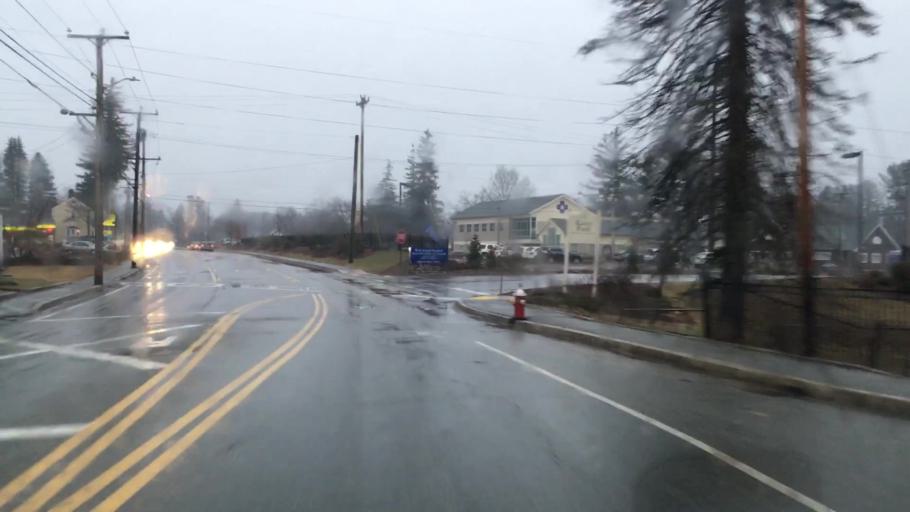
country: US
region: New Hampshire
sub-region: Hillsborough County
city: Milford
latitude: 42.8282
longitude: -71.6327
